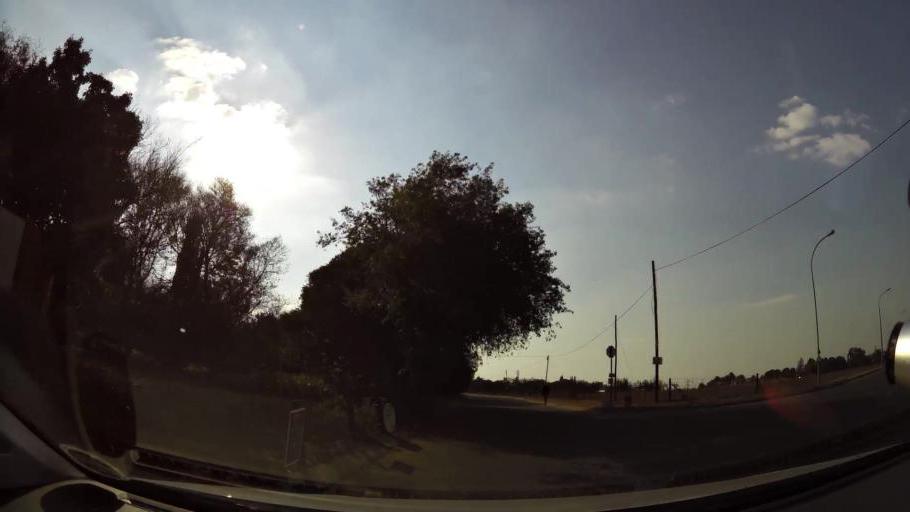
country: ZA
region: Gauteng
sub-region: City of Johannesburg Metropolitan Municipality
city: Modderfontein
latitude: -26.0794
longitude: 28.2019
